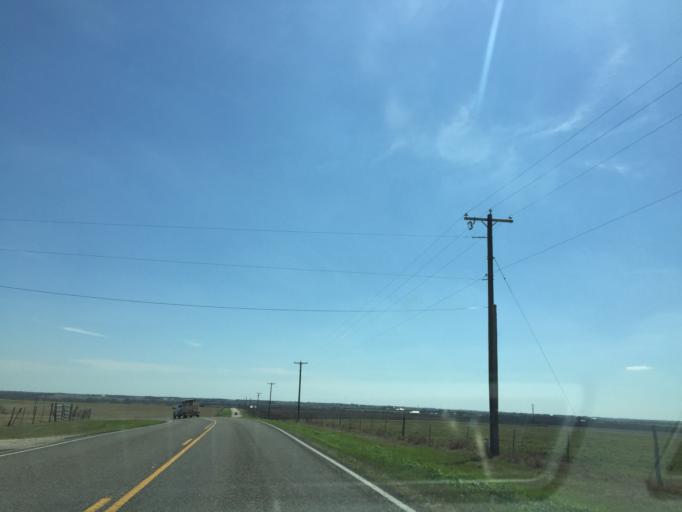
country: US
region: Texas
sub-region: Williamson County
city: Taylor
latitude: 30.5558
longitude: -97.3236
